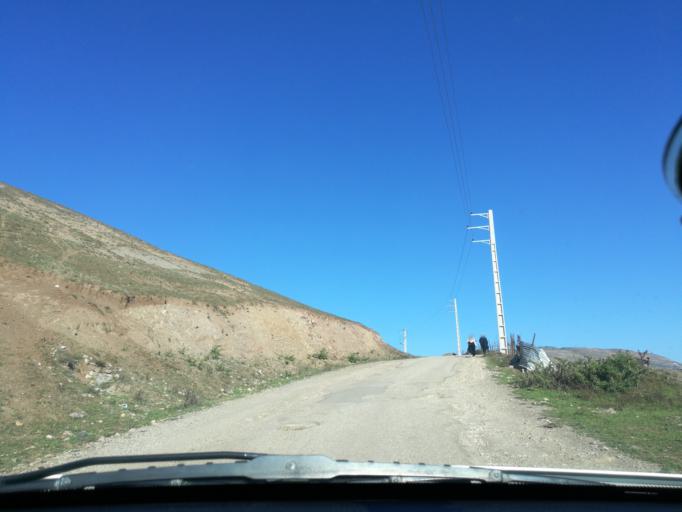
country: IR
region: Mazandaran
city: `Abbasabad
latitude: 36.5589
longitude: 51.1919
